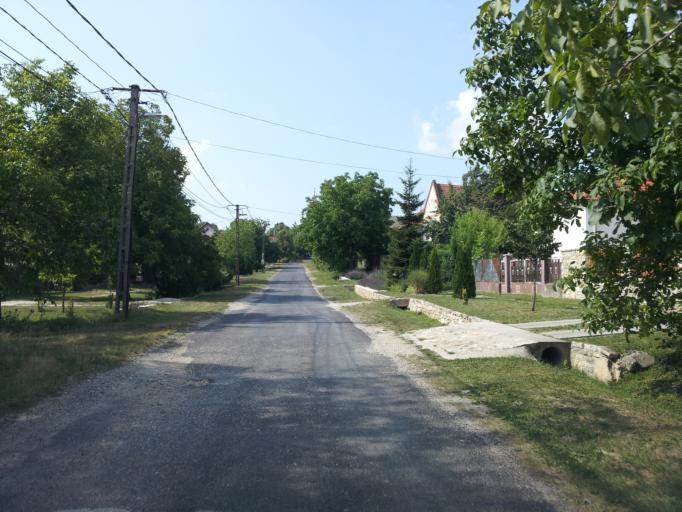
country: HU
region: Veszprem
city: Balatonfured
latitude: 47.0020
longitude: 17.8304
